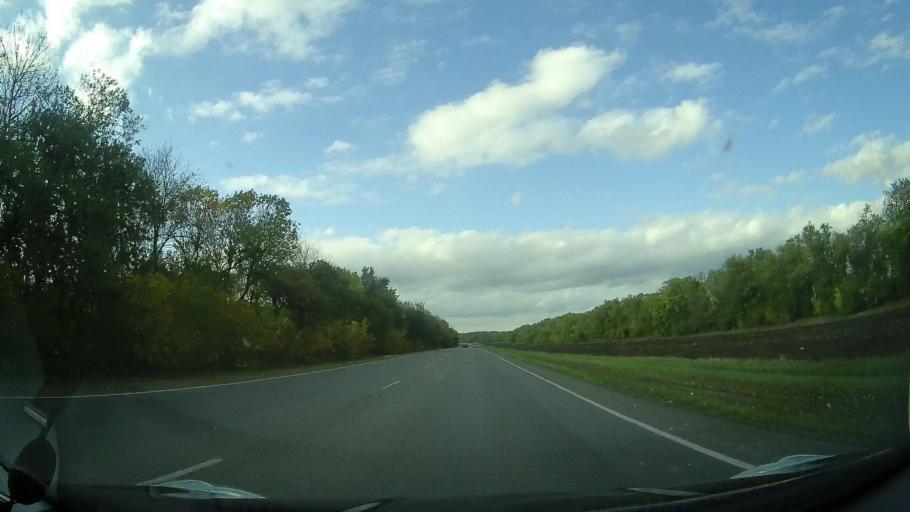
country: RU
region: Rostov
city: Kirovskaya
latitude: 46.9545
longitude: 40.0785
